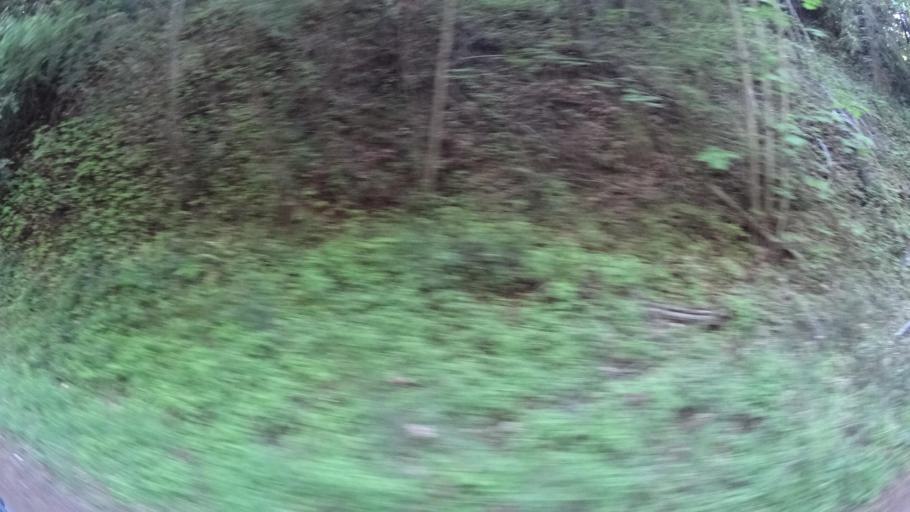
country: US
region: California
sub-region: Humboldt County
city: Rio Dell
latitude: 40.4432
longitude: -123.9721
